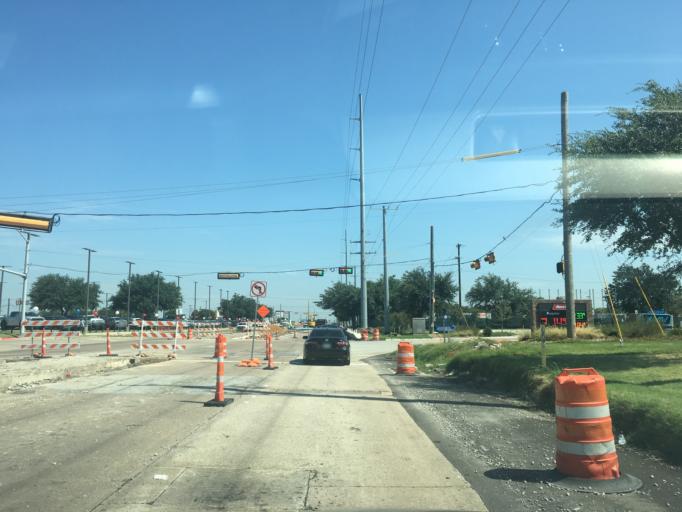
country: US
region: Texas
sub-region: Dallas County
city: Garland
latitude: 32.8738
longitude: -96.6654
